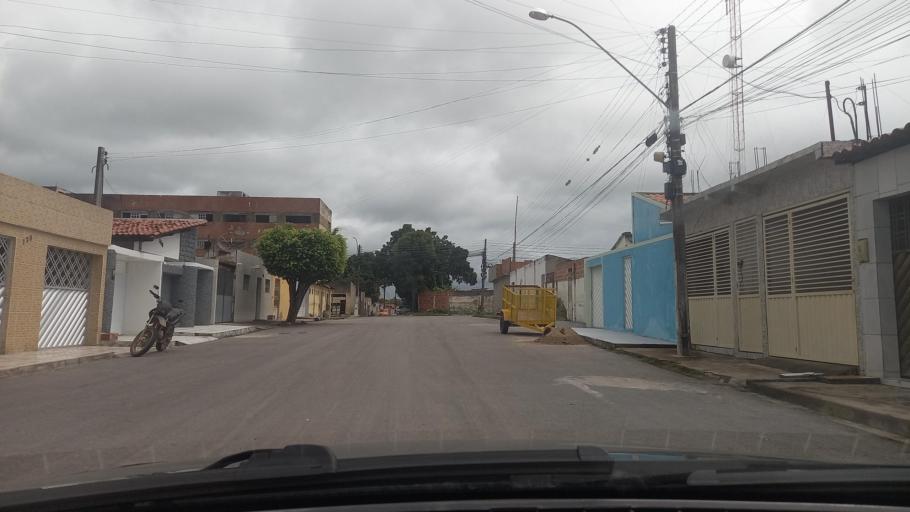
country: BR
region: Alagoas
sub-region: Delmiro Gouveia
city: Delmiro Gouveia
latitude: -9.3908
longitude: -37.9974
